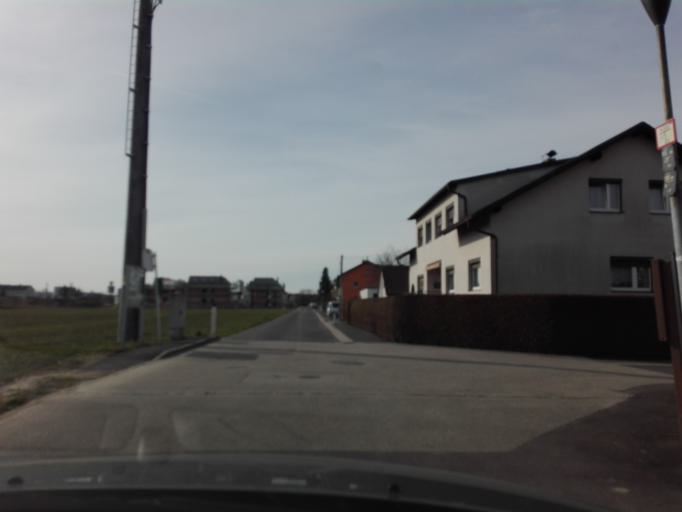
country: AT
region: Upper Austria
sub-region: Politischer Bezirk Linz-Land
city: Ansfelden
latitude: 48.2204
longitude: 14.2831
